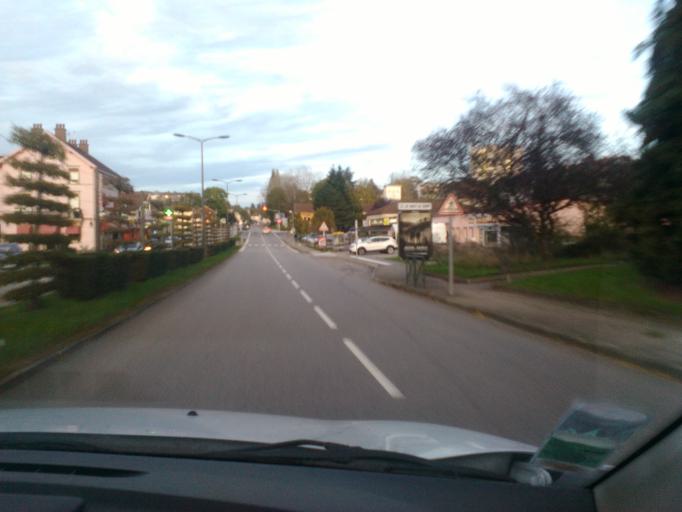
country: FR
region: Lorraine
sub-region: Departement des Vosges
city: Epinal
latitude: 48.1927
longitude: 6.4521
